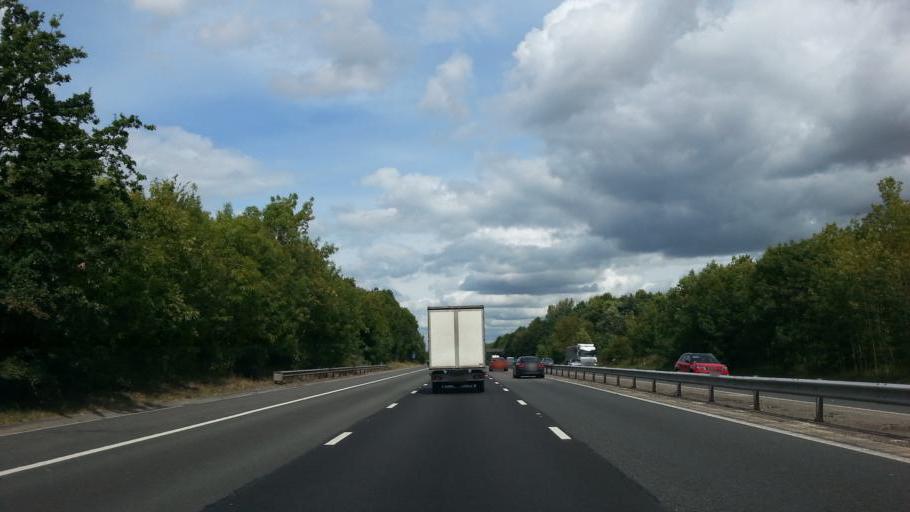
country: GB
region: England
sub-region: Hertfordshire
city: Sawbridgeworth
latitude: 51.7794
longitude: 0.1659
